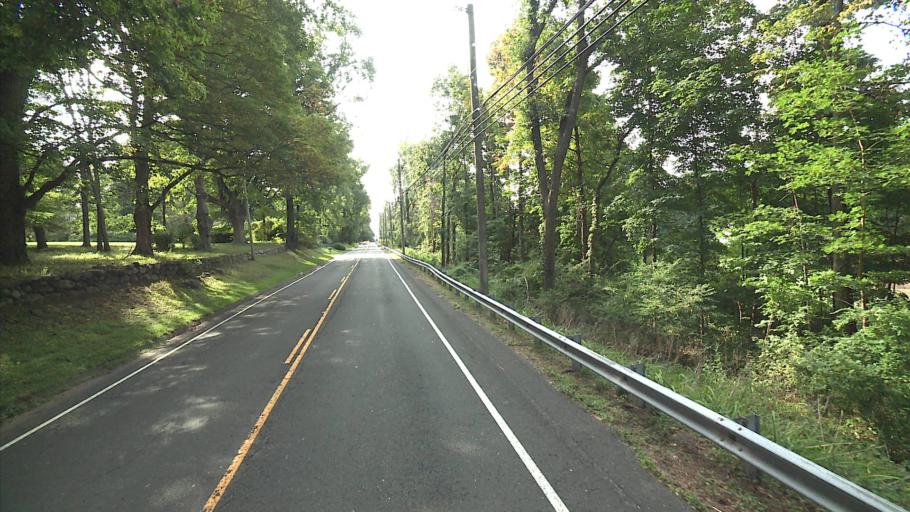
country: US
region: Connecticut
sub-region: Fairfield County
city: New Canaan
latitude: 41.1767
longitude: -73.4981
